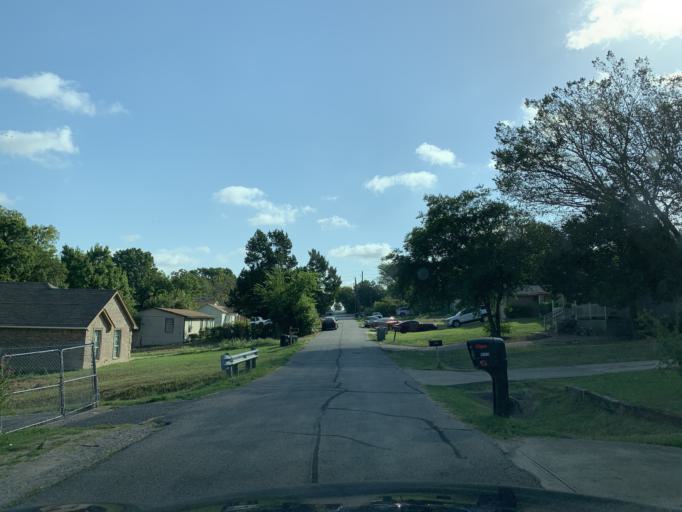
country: US
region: Texas
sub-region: Dallas County
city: Hutchins
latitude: 32.6757
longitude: -96.7785
